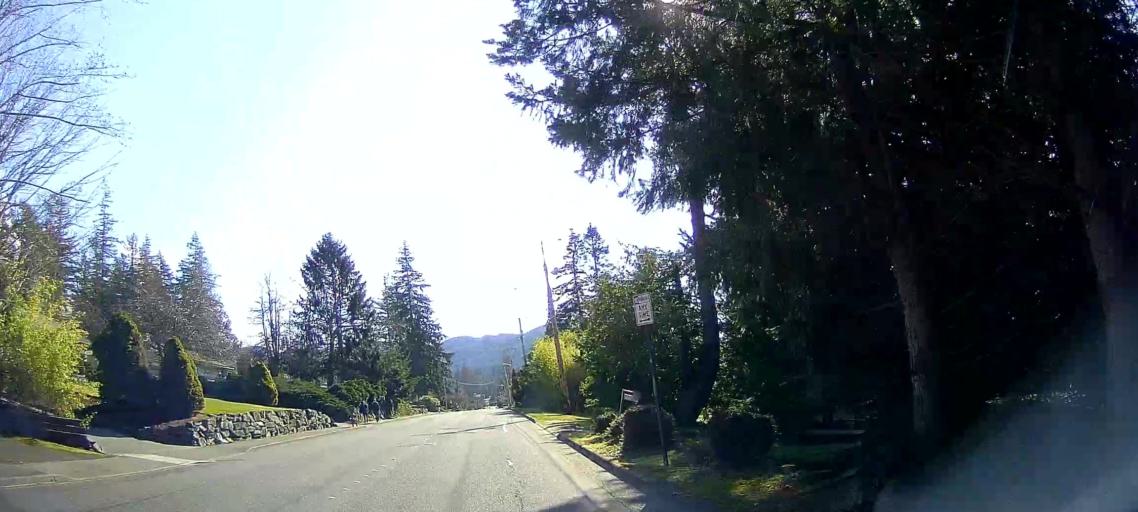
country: US
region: Washington
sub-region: Whatcom County
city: Bellingham
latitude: 48.7215
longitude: -122.4755
